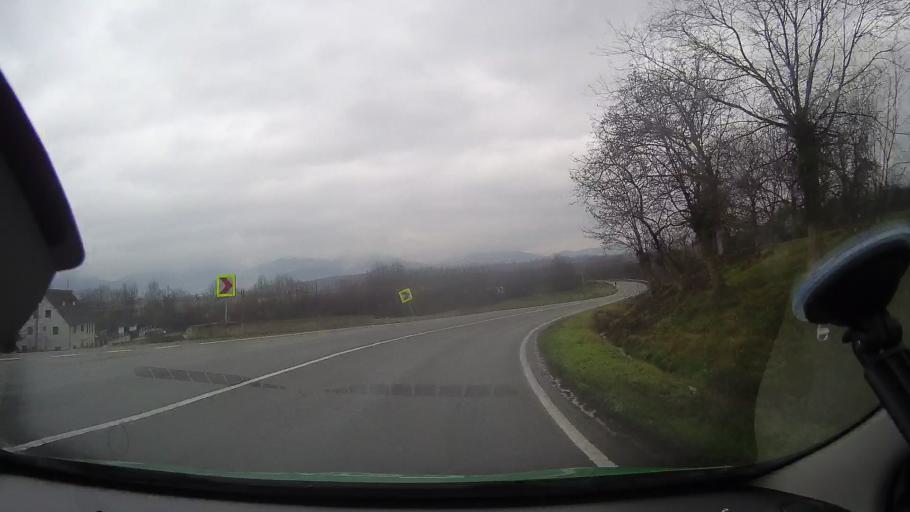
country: RO
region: Arad
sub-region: Comuna Gurahont
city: Gurahont
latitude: 46.2740
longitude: 22.3085
